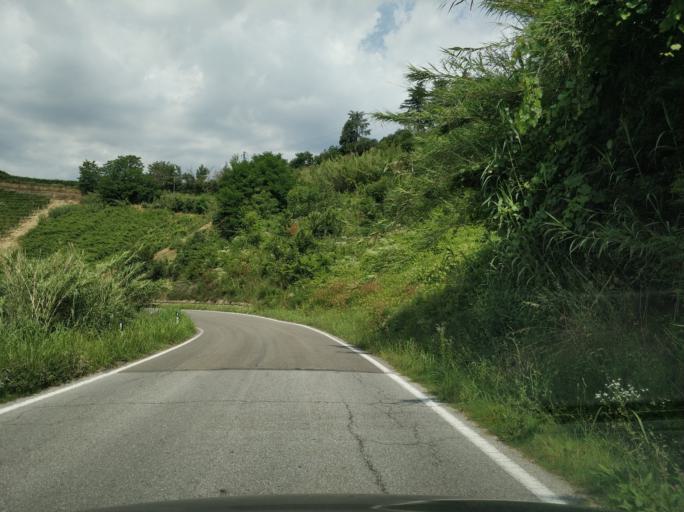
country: IT
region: Piedmont
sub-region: Provincia di Cuneo
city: Santo Stefano Roero
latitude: 44.7868
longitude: 7.9572
